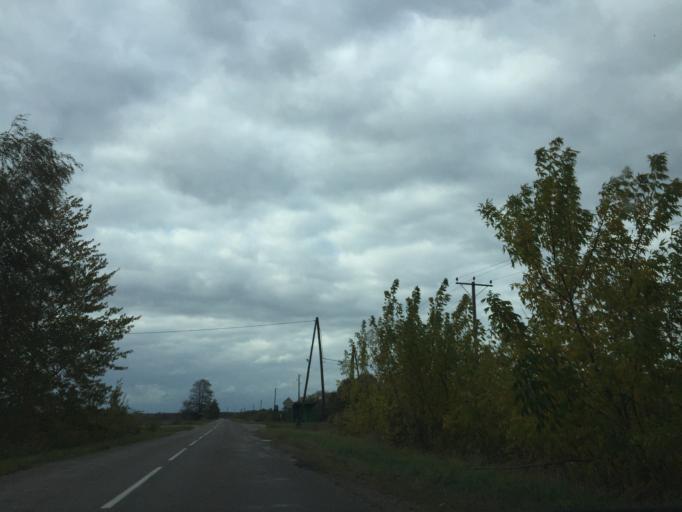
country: LV
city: Tireli
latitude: 56.8054
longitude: 23.5905
